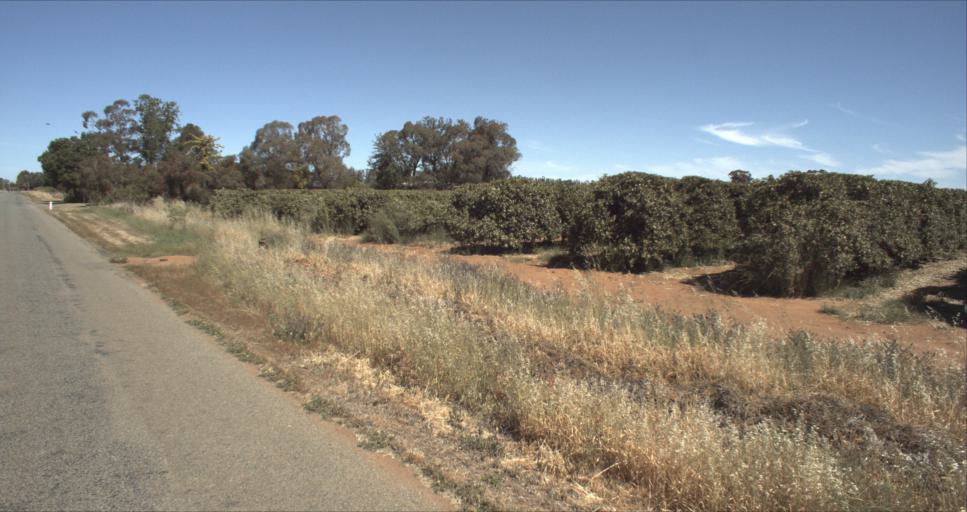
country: AU
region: New South Wales
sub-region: Leeton
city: Leeton
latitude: -34.5429
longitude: 146.3651
